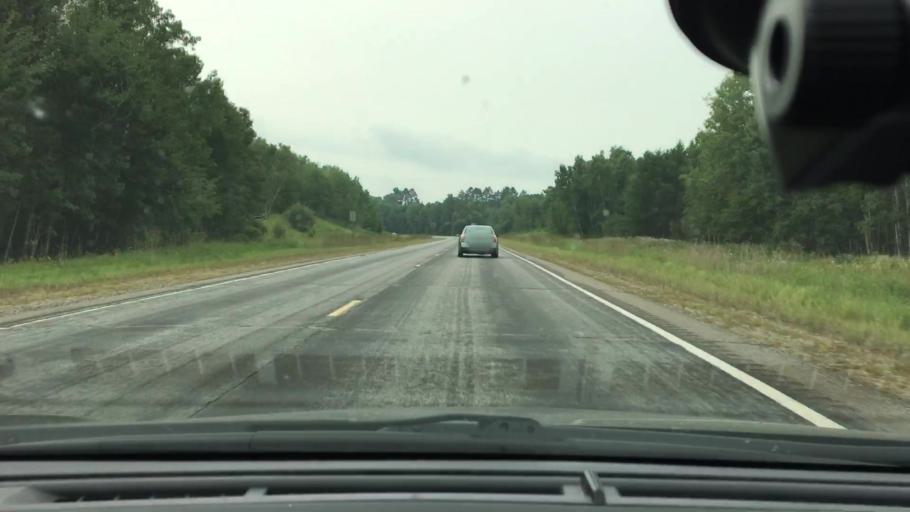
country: US
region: Minnesota
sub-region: Crow Wing County
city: Cross Lake
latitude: 46.6598
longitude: -93.9547
